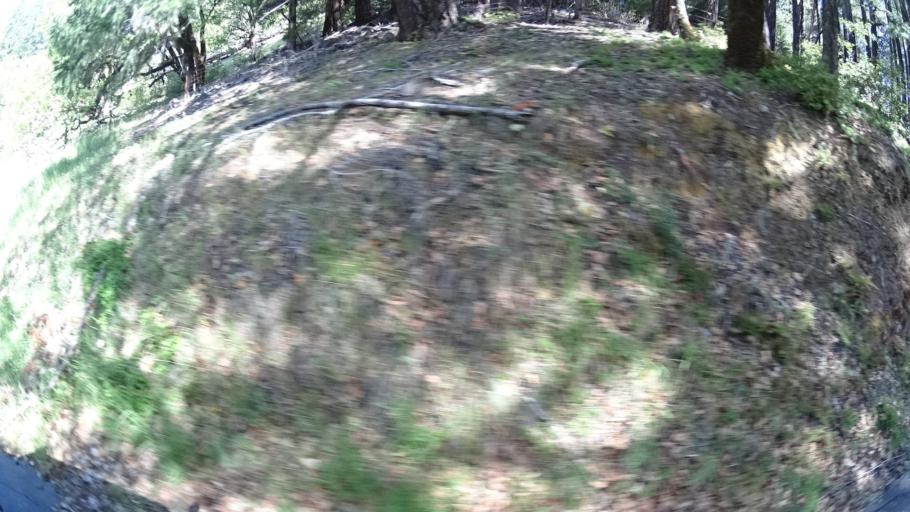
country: US
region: California
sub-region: Humboldt County
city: Redway
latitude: 40.0775
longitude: -123.6537
